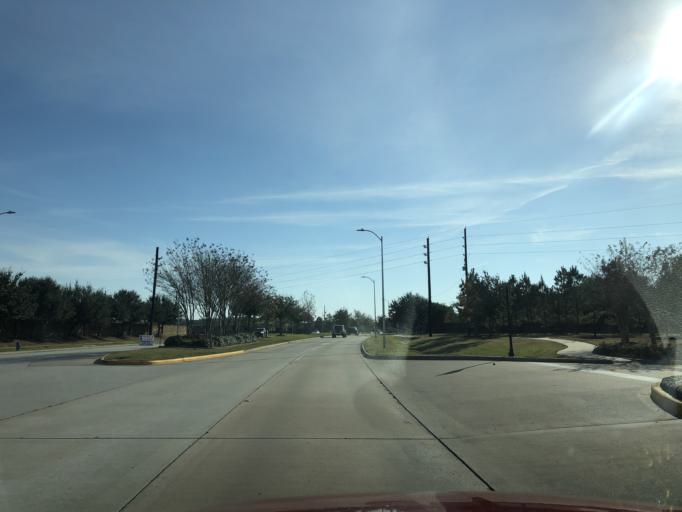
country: US
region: Texas
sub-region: Harris County
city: Tomball
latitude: 30.0550
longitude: -95.5723
